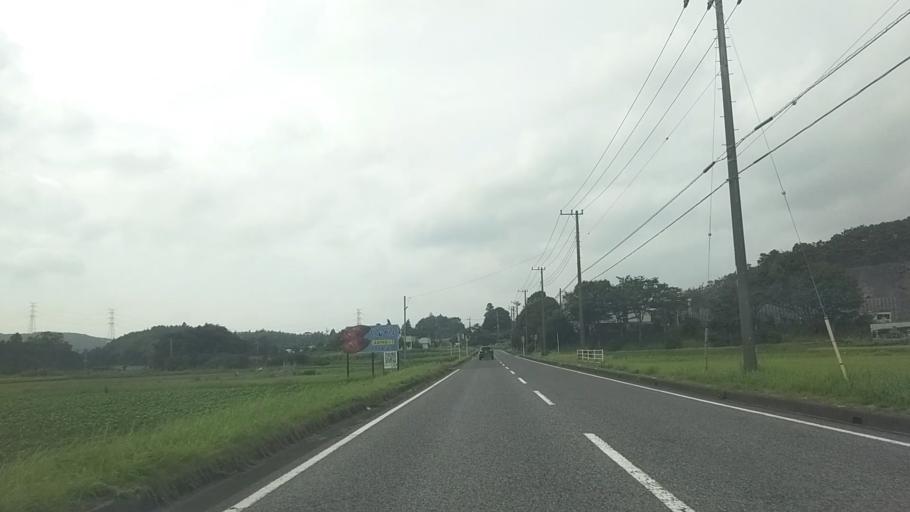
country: JP
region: Chiba
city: Kimitsu
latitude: 35.2748
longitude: 139.9948
